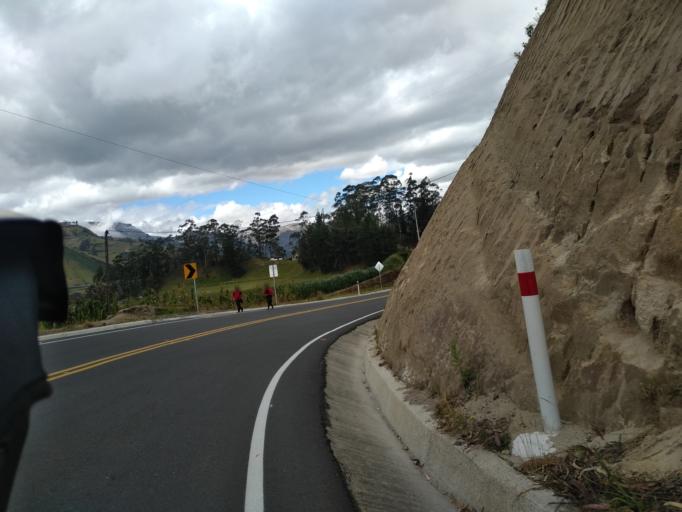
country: EC
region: Cotopaxi
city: Saquisili
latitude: -0.7715
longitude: -78.9090
